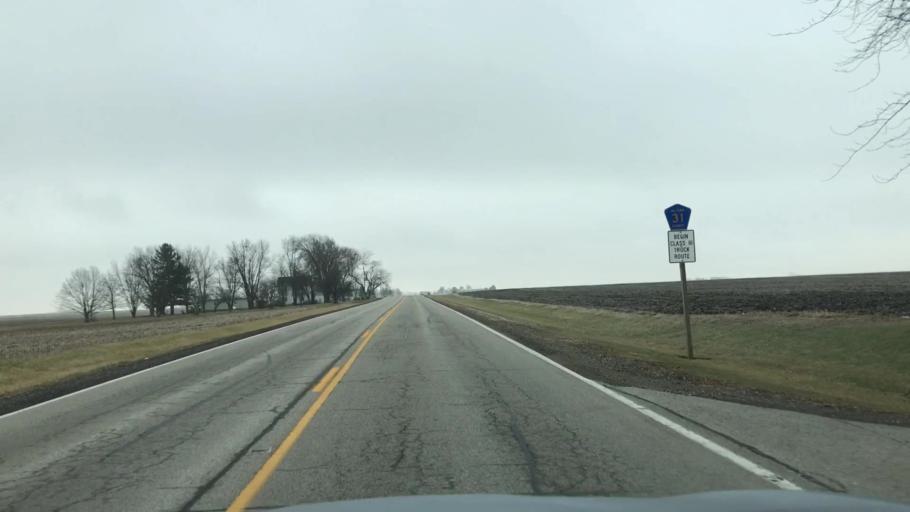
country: US
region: Illinois
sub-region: McLean County
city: Hudson
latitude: 40.6052
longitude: -88.9451
